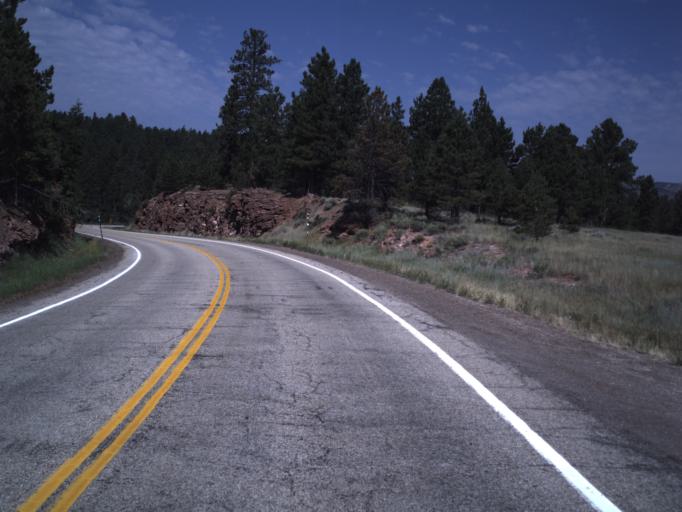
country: US
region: Utah
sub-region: Daggett County
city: Manila
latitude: 40.8574
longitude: -109.6815
